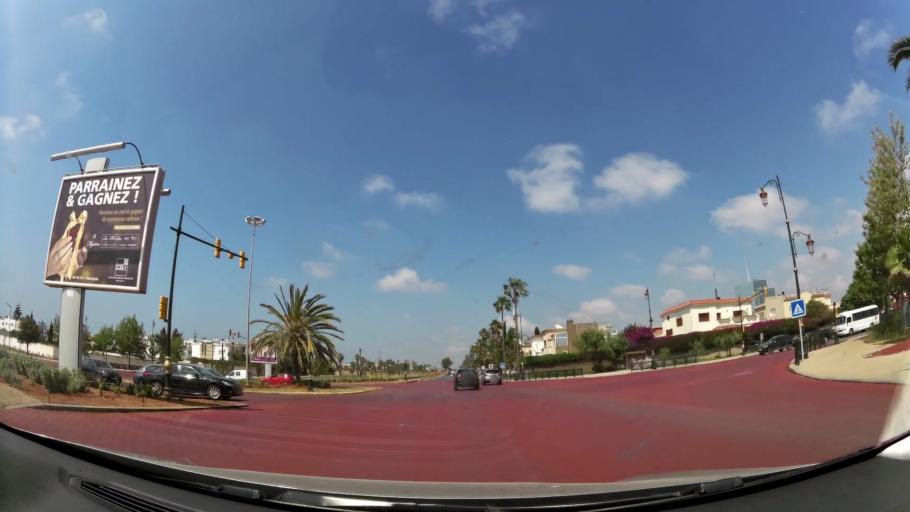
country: MA
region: Rabat-Sale-Zemmour-Zaer
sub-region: Skhirate-Temara
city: Temara
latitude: 33.9573
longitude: -6.8778
